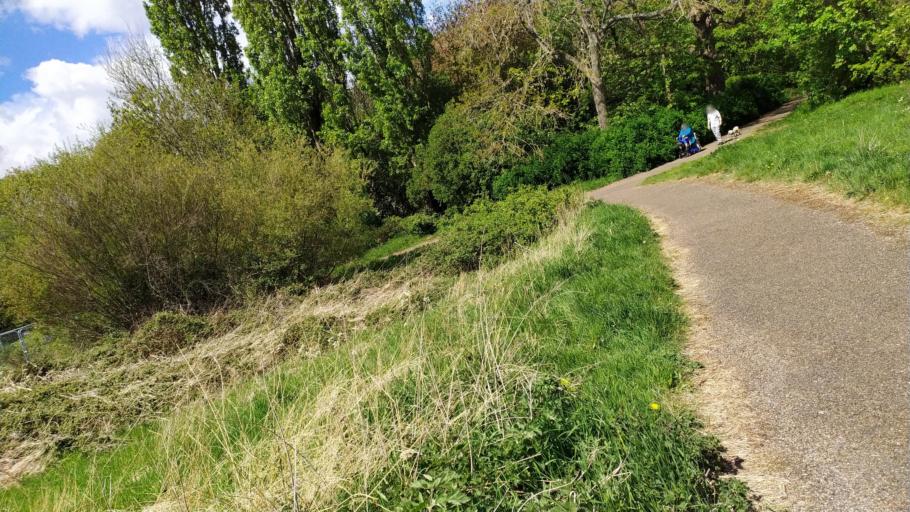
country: GB
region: England
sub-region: City and Borough of Leeds
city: Shadwell
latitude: 53.8080
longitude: -1.4839
